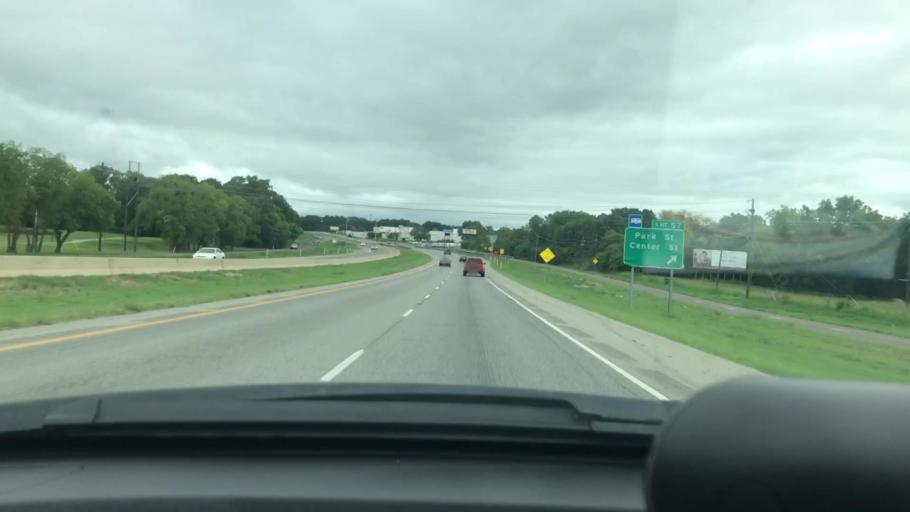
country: US
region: Texas
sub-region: Grayson County
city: Sherman
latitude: 33.6087
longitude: -96.6093
